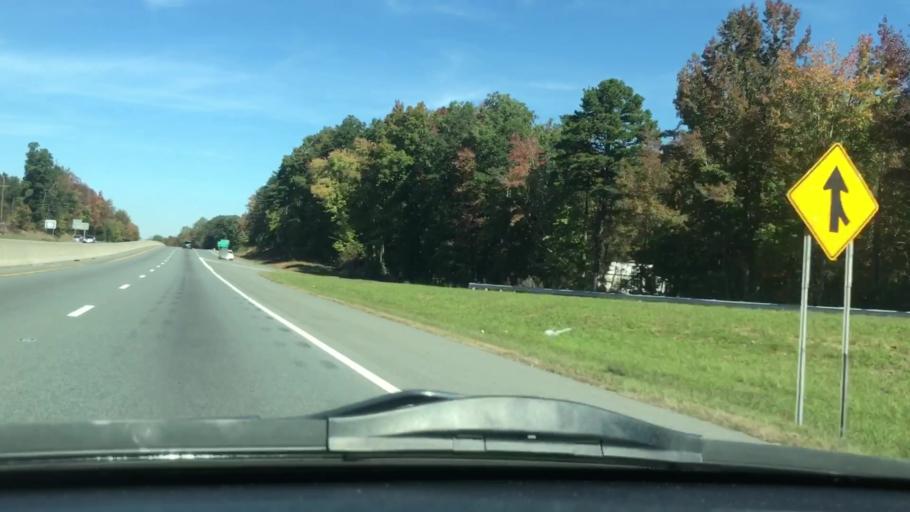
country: US
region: North Carolina
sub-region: Randolph County
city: Asheboro
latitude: 35.7209
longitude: -79.8258
